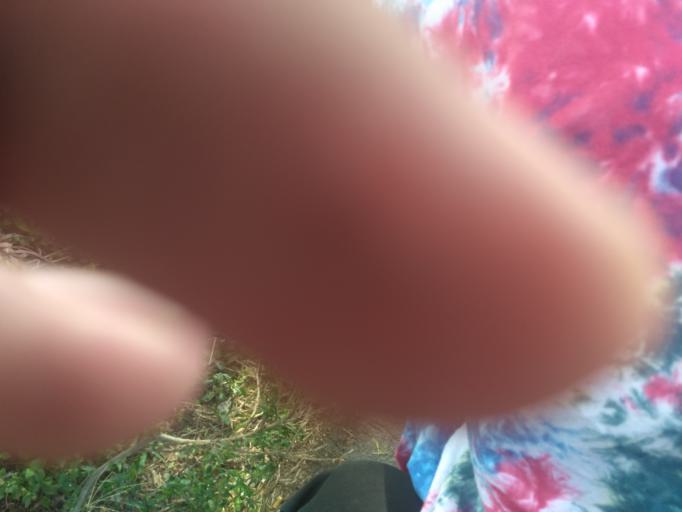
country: ID
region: Daerah Istimewa Yogyakarta
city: Godean
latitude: -7.7461
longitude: 110.3200
